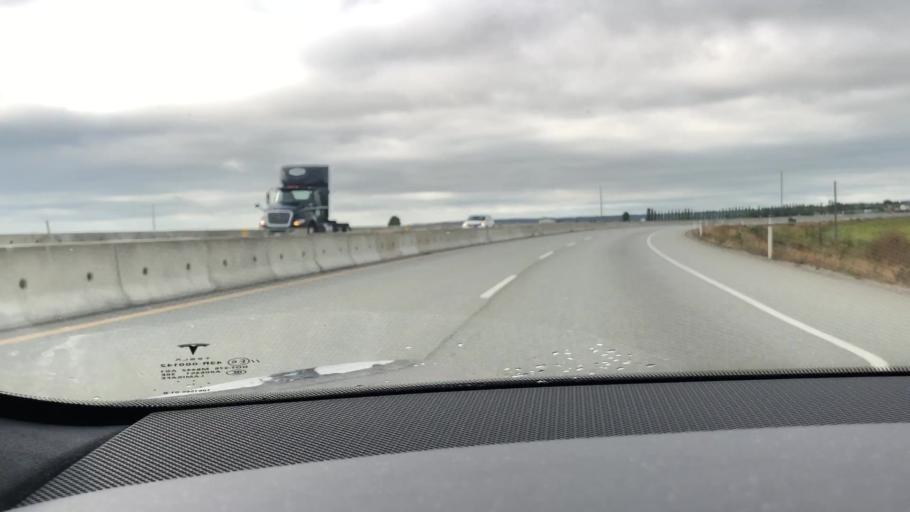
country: CA
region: British Columbia
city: Ladner
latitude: 49.0630
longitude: -123.0370
